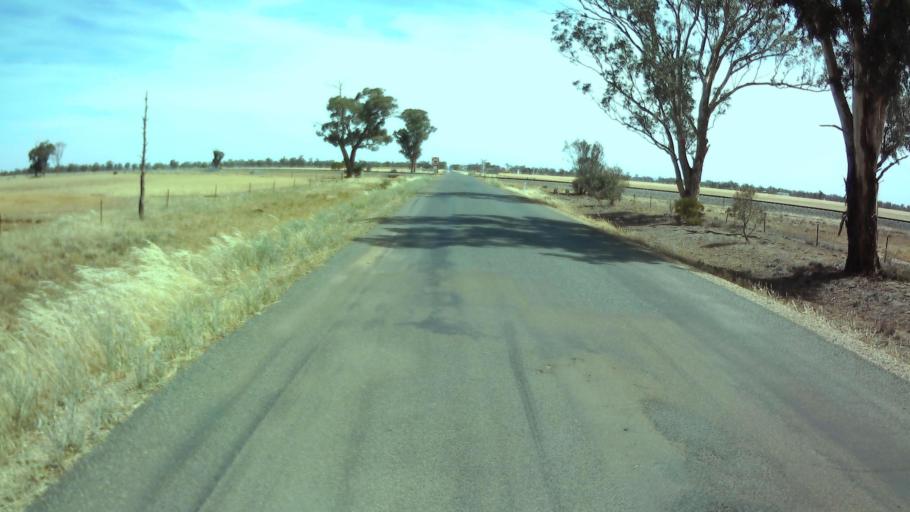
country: AU
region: New South Wales
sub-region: Weddin
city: Grenfell
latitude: -33.9826
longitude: 147.7776
